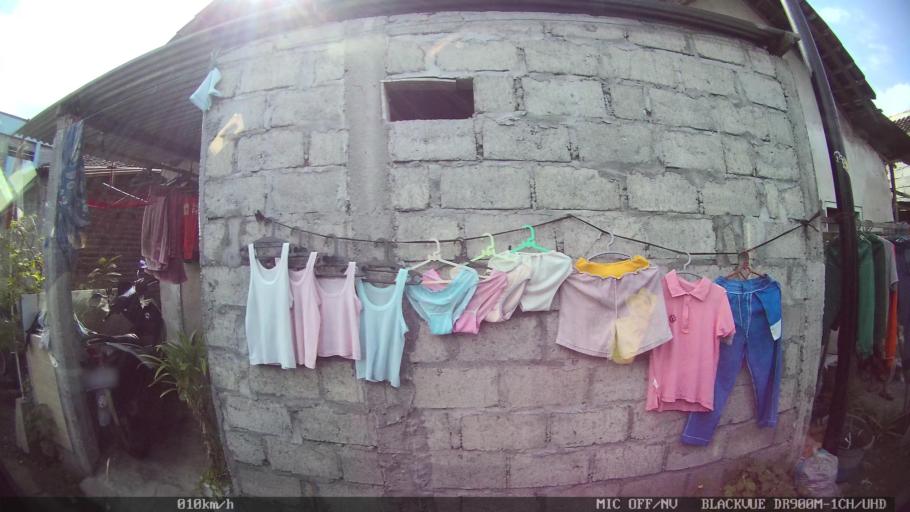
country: ID
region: Daerah Istimewa Yogyakarta
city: Kasihan
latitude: -7.8325
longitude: 110.3646
